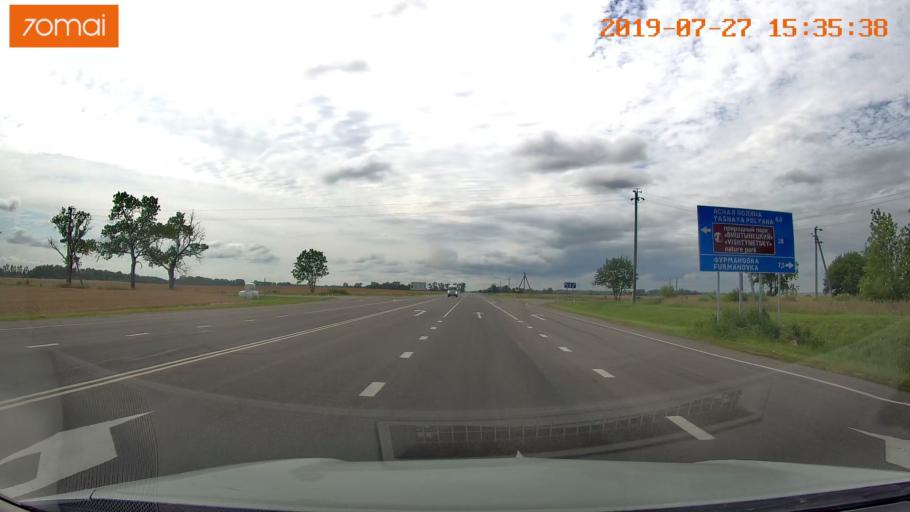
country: RU
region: Kaliningrad
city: Nesterov
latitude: 54.6133
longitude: 22.3917
